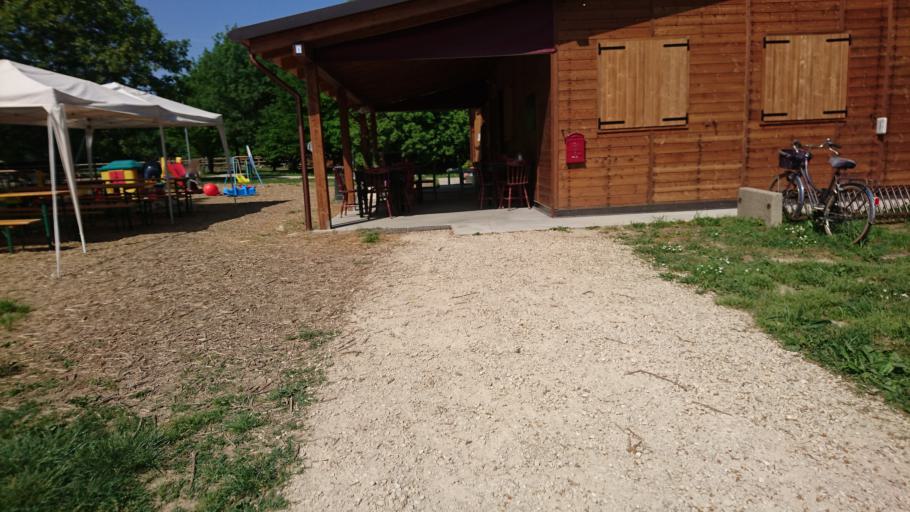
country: IT
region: Veneto
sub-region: Provincia di Padova
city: Padova
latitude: 45.4260
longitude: 11.9025
